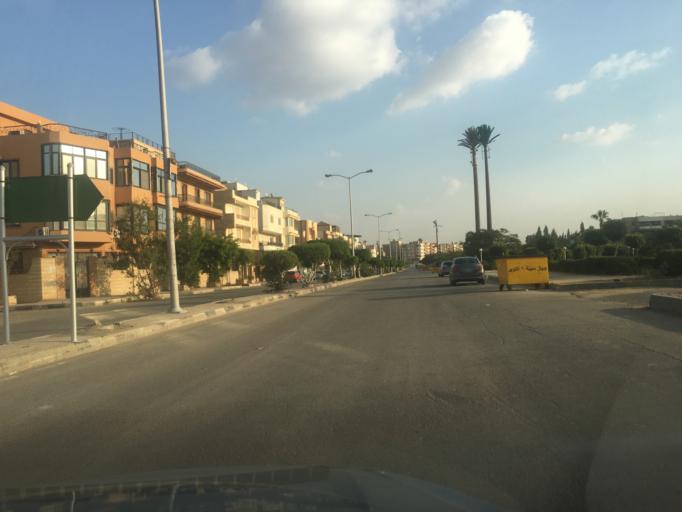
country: EG
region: Al Jizah
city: Madinat Sittah Uktubar
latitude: 29.9880
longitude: 30.9414
